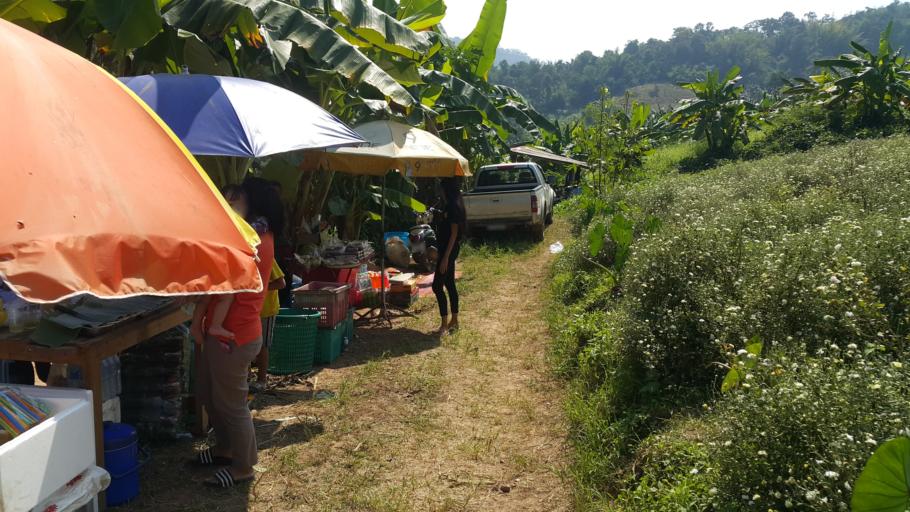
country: TH
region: Chiang Mai
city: Samoeng
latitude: 18.9309
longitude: 98.6157
